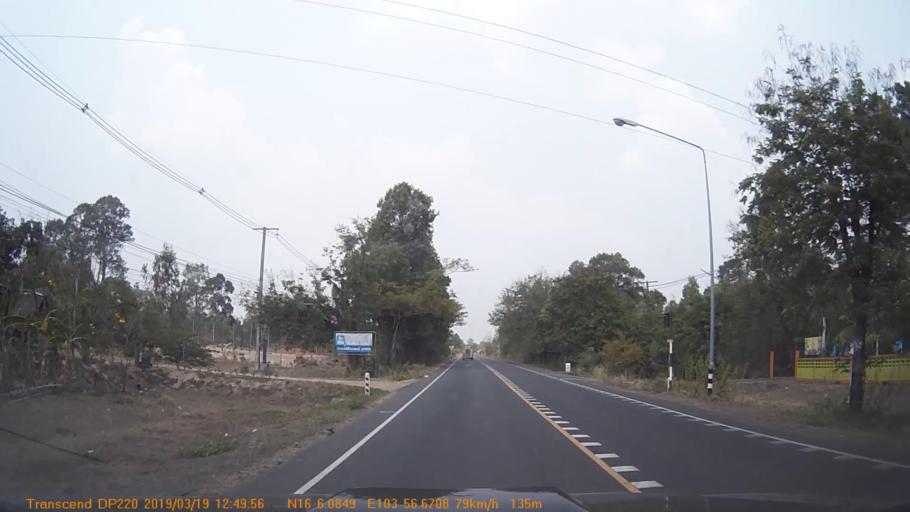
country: TH
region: Roi Et
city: Selaphum
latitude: 16.1019
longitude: 103.9446
